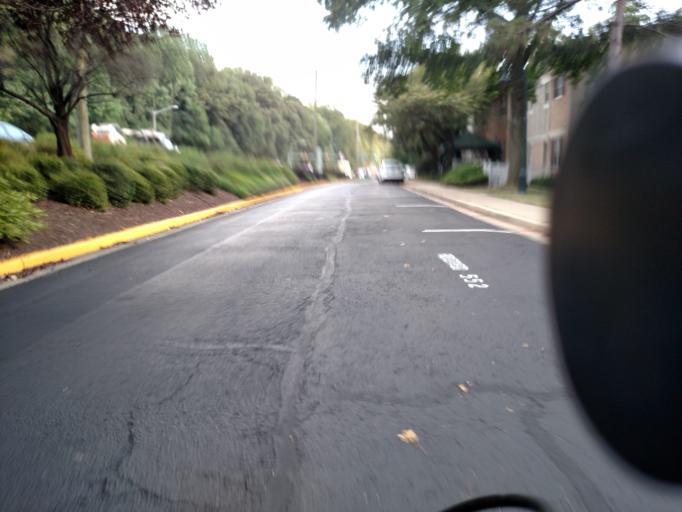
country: US
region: Virginia
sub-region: Fairfax County
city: Merrifield
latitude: 38.8603
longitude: -77.2268
